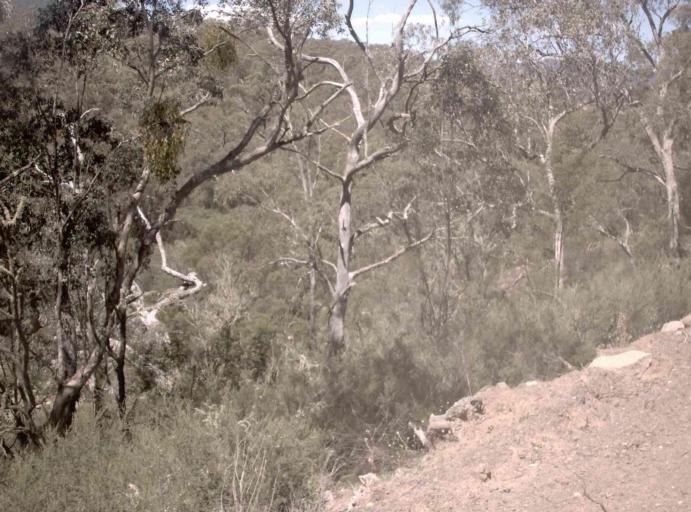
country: AU
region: New South Wales
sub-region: Snowy River
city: Jindabyne
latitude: -37.0349
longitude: 148.5424
